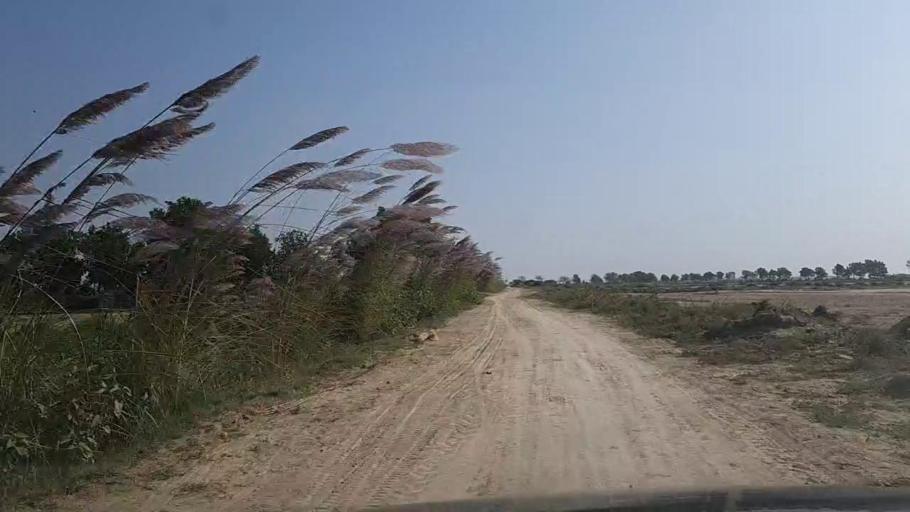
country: PK
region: Sindh
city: Gharo
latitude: 24.7170
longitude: 67.5676
